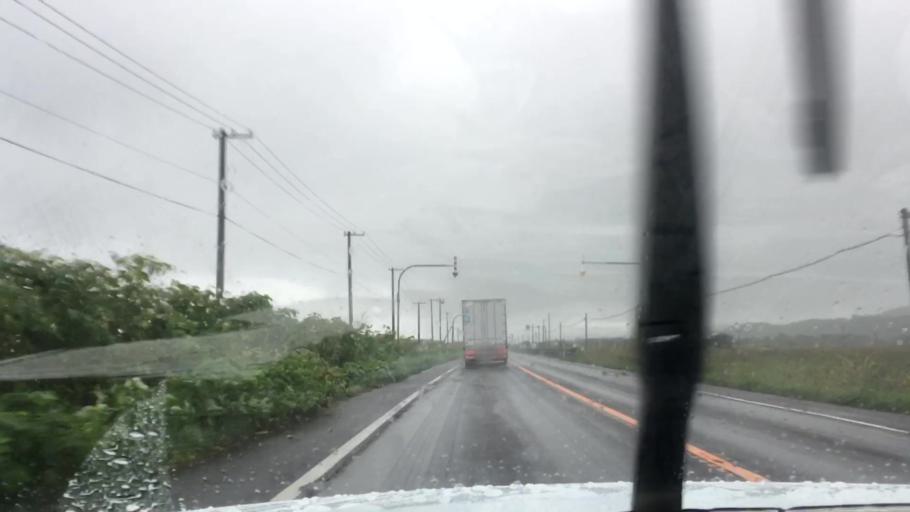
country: JP
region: Hokkaido
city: Niseko Town
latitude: 42.4271
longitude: 140.3165
